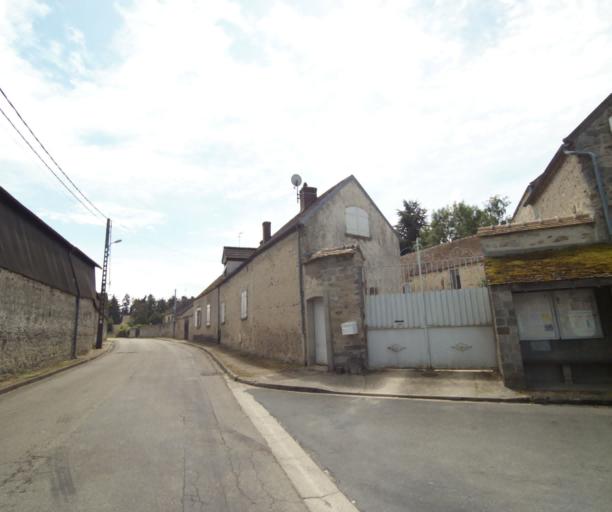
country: FR
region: Ile-de-France
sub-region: Departement de Seine-et-Marne
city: Arbonne-la-Foret
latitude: 48.4406
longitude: 2.5613
